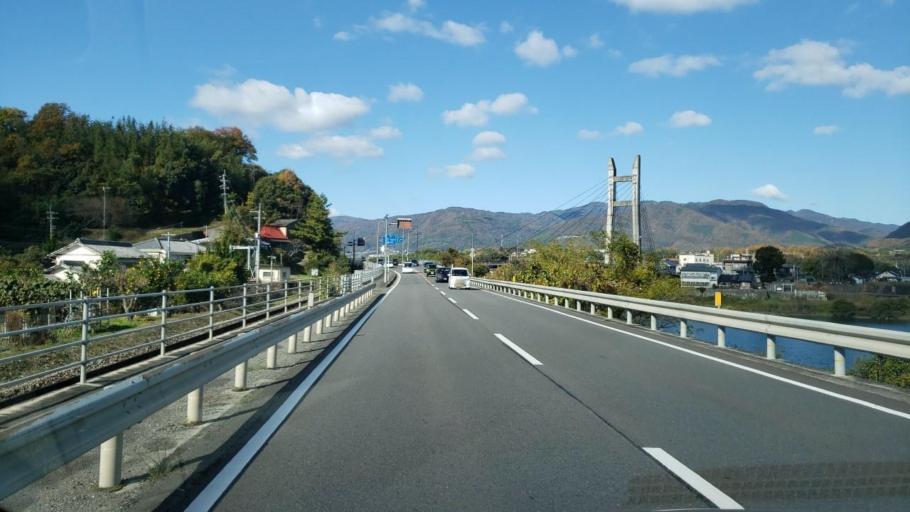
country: JP
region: Tokushima
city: Wakimachi
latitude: 34.0634
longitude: 134.1969
